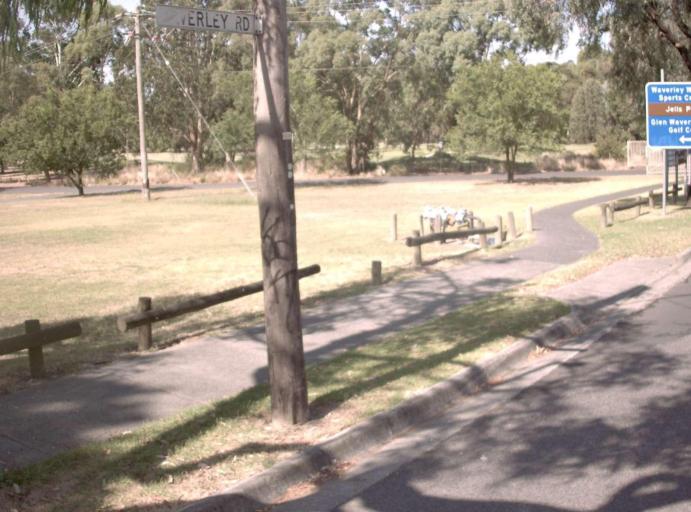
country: AU
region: Victoria
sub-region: Monash
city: Mulgrave
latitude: -37.8919
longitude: 145.1914
